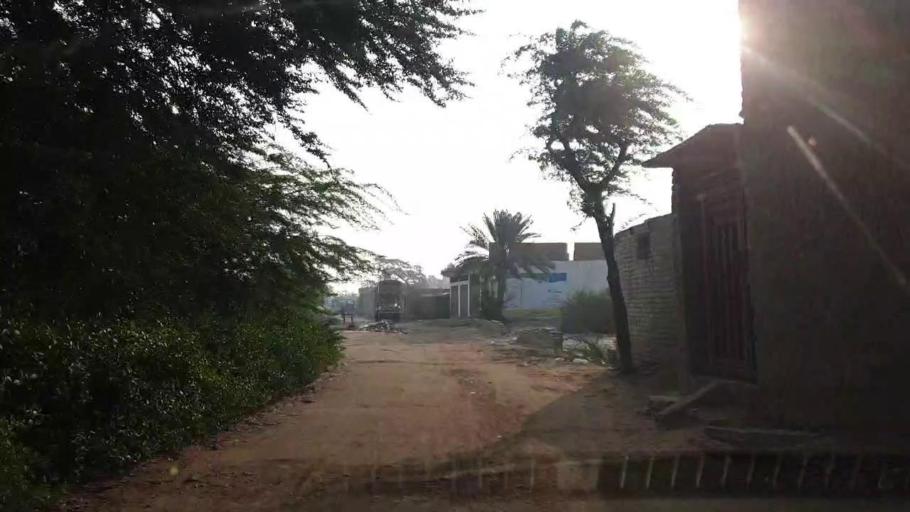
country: PK
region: Sindh
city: Tando Muhammad Khan
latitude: 25.1263
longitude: 68.5426
